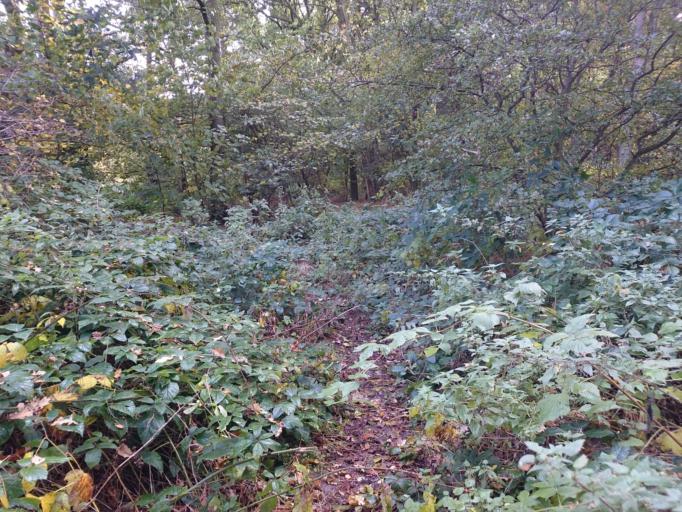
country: DK
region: Central Jutland
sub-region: Arhus Kommune
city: Stavtrup
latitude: 56.1420
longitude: 10.0928
